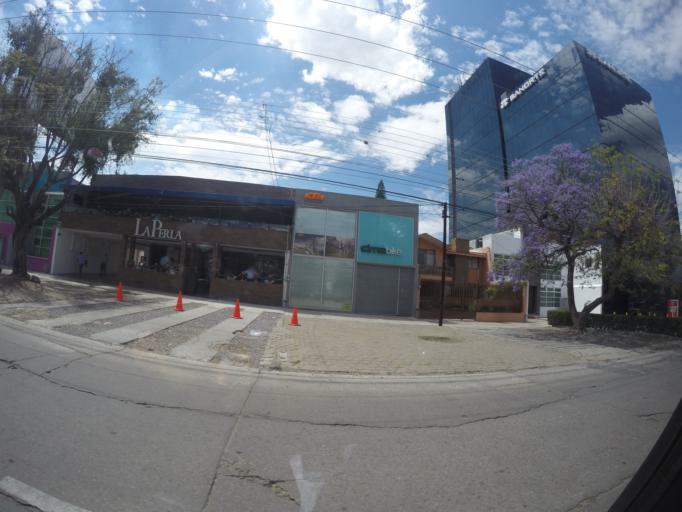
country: MX
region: Guanajuato
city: Leon
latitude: 21.1454
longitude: -101.6906
